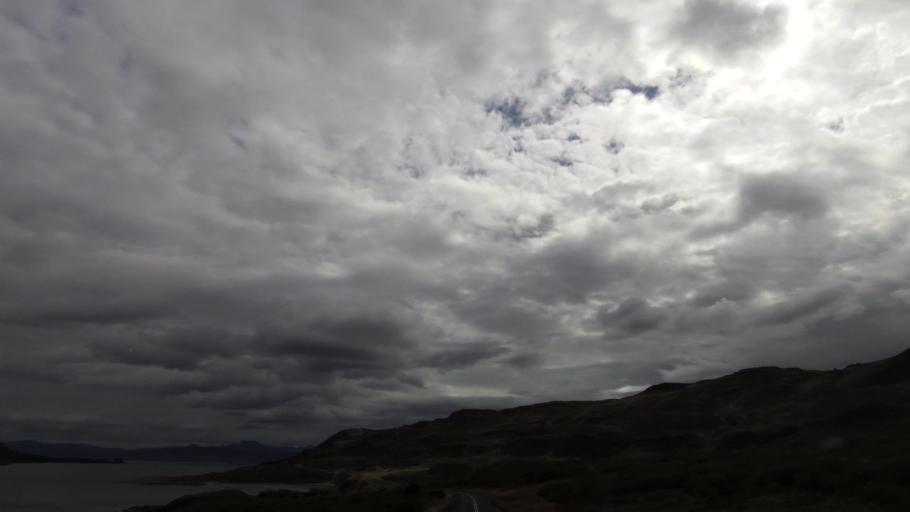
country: IS
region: West
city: Stykkisholmur
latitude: 65.5360
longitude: -22.1222
